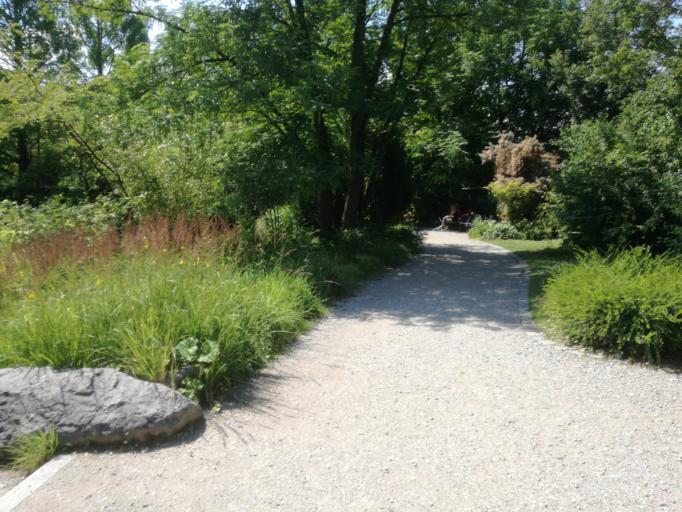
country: DE
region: Bavaria
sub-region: Upper Bavaria
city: Neuried
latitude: 48.1233
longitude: 11.5125
